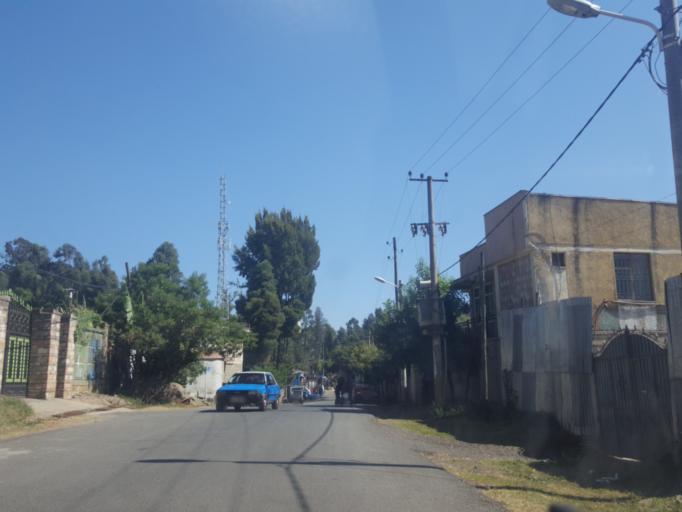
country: ET
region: Adis Abeba
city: Addis Ababa
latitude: 9.0543
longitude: 38.7377
